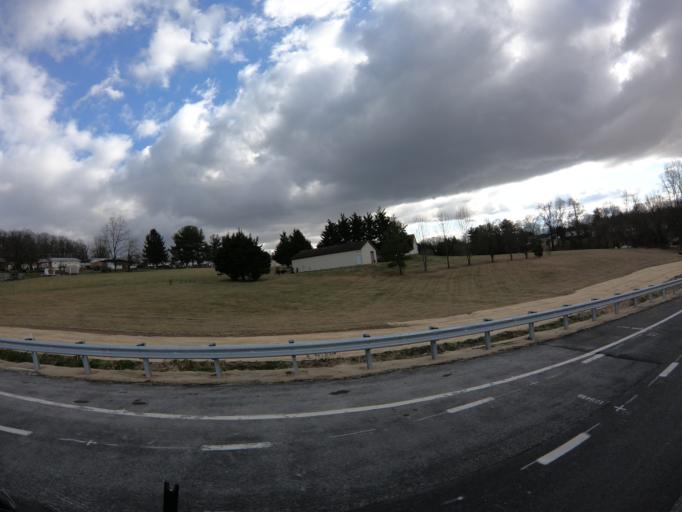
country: US
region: Maryland
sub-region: Frederick County
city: Walkersville
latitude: 39.4553
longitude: -77.3112
